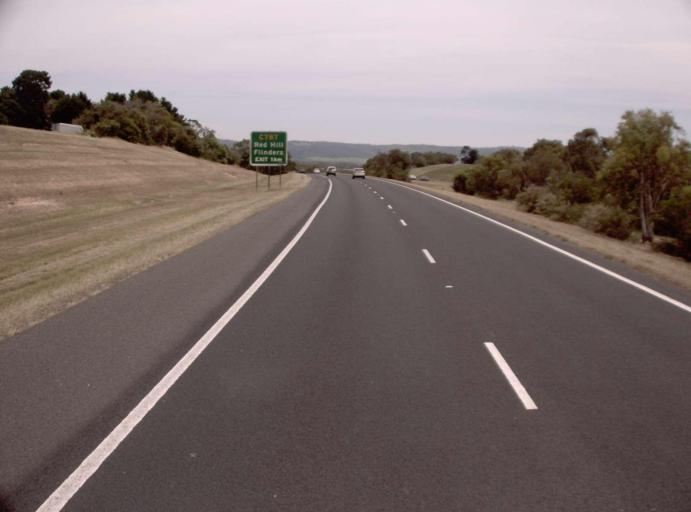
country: AU
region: Victoria
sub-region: Mornington Peninsula
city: Mount Martha
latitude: -38.2918
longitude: 145.0427
